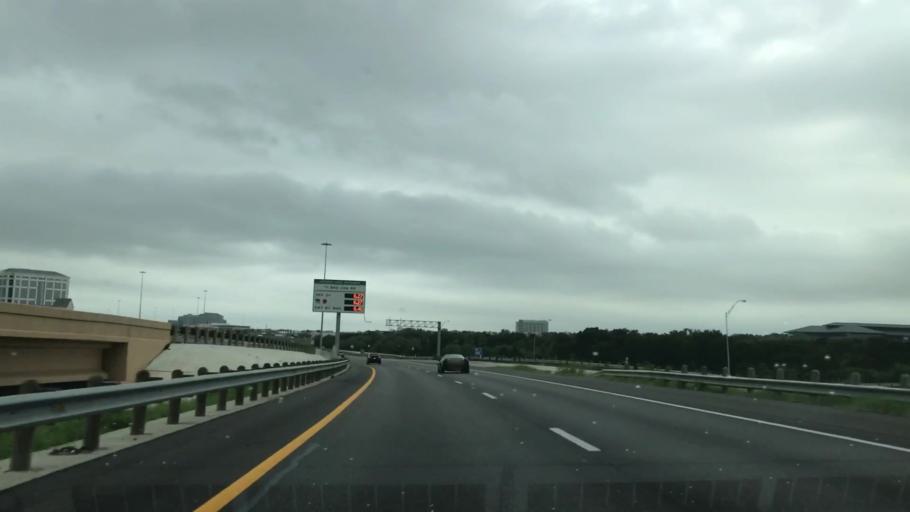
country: US
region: Texas
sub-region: Dallas County
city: Irving
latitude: 32.8822
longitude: -96.9488
